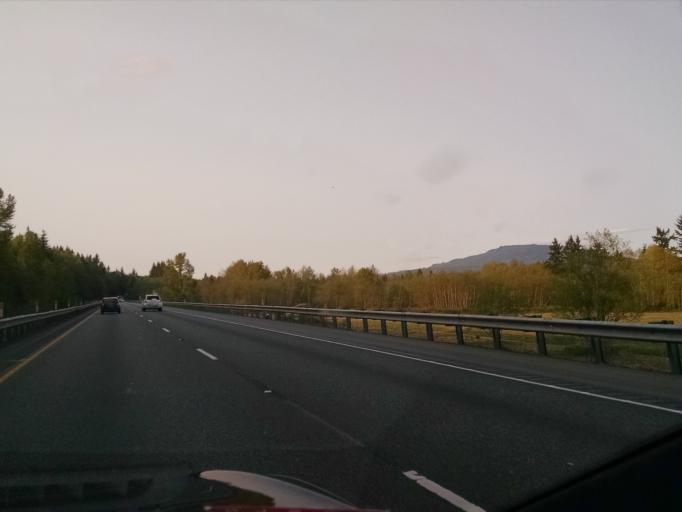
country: US
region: Washington
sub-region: Skagit County
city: Burlington
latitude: 48.5350
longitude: -122.3519
